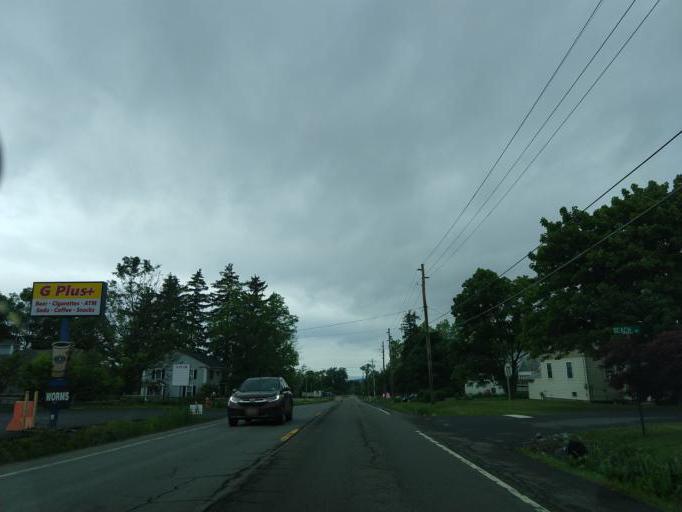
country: US
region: New York
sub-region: Tompkins County
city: Lansing
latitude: 42.5388
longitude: -76.5107
